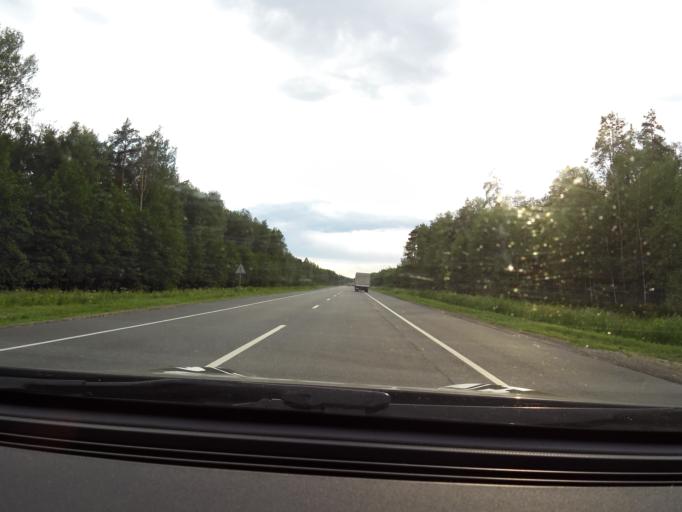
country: RU
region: Vladimir
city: Raduzhnyy
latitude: 56.0651
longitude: 40.3510
